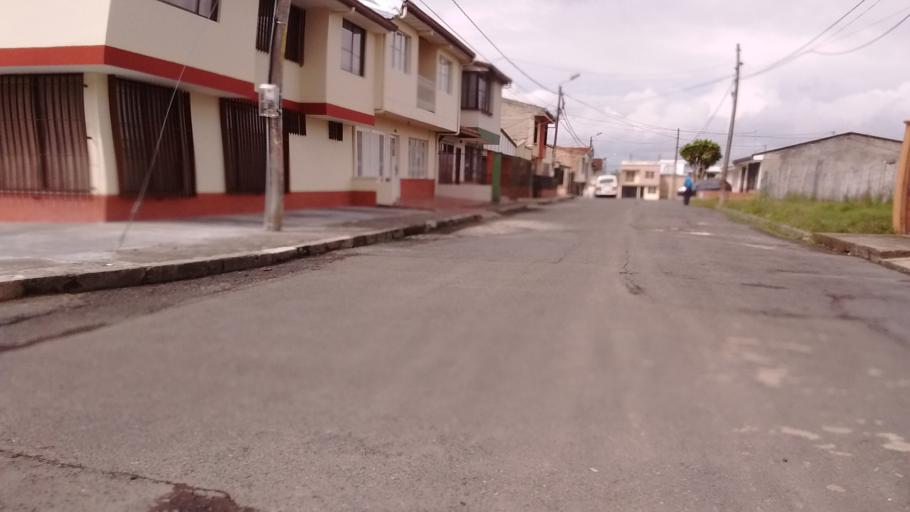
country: CO
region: Cauca
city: Popayan
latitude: 2.4544
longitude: -76.6047
